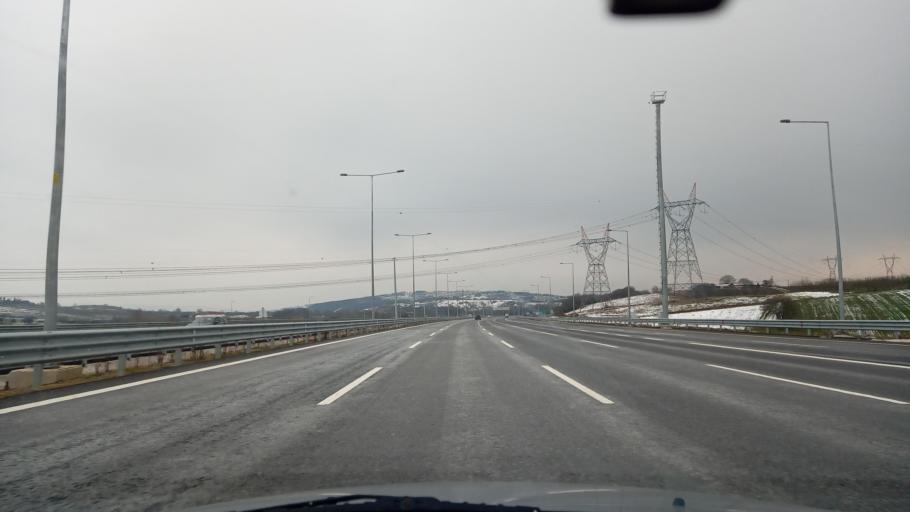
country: TR
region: Kocaeli
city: Akmese
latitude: 40.8462
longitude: 30.2228
